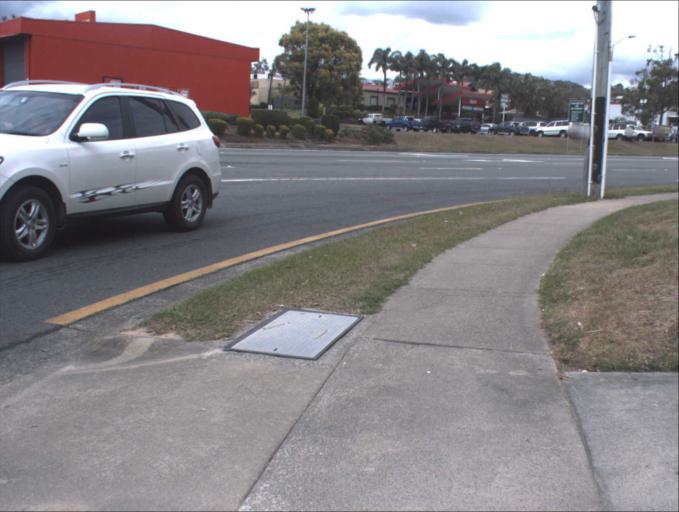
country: AU
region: Queensland
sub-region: Logan
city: Slacks Creek
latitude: -27.6623
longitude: 153.1743
